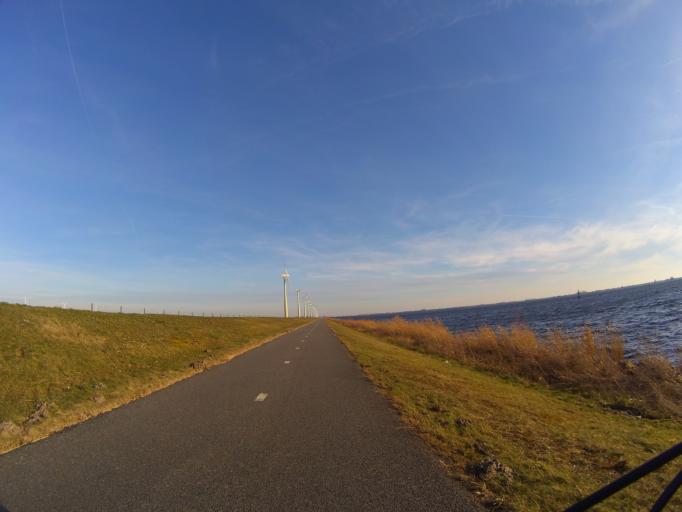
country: NL
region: Utrecht
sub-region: Gemeente Bunschoten
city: Spakenburg
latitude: 52.2910
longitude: 5.3398
